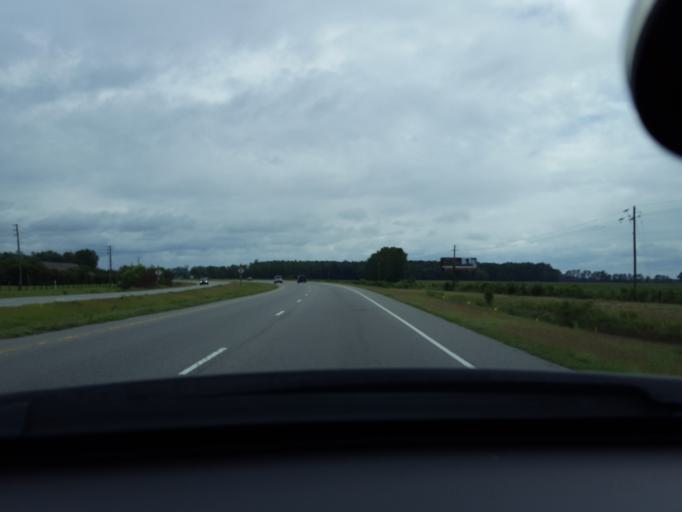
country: US
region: North Carolina
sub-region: Pitt County
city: Ayden
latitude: 35.4665
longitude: -77.4359
